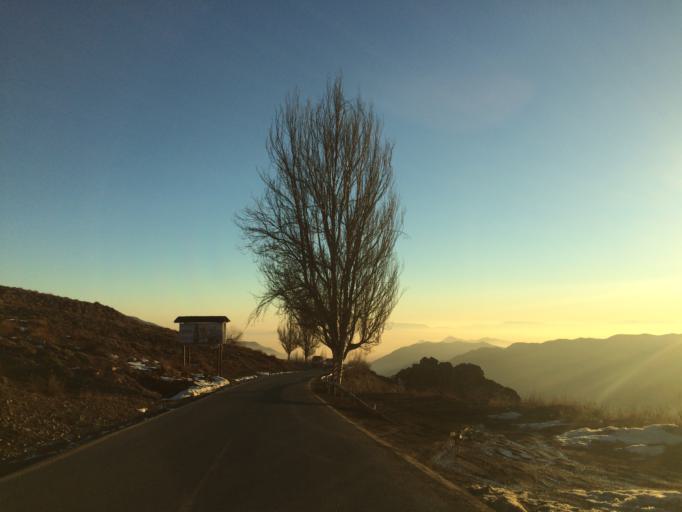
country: CL
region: Santiago Metropolitan
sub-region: Provincia de Santiago
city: Villa Presidente Frei, Nunoa, Santiago, Chile
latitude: -33.3446
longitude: -70.3008
